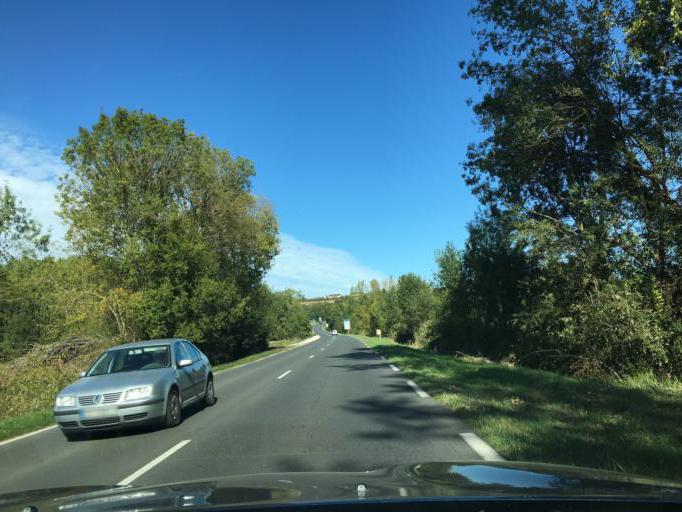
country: FR
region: Centre
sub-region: Departement d'Indre-et-Loire
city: Azay-le-Rideau
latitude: 47.2577
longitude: 0.4563
